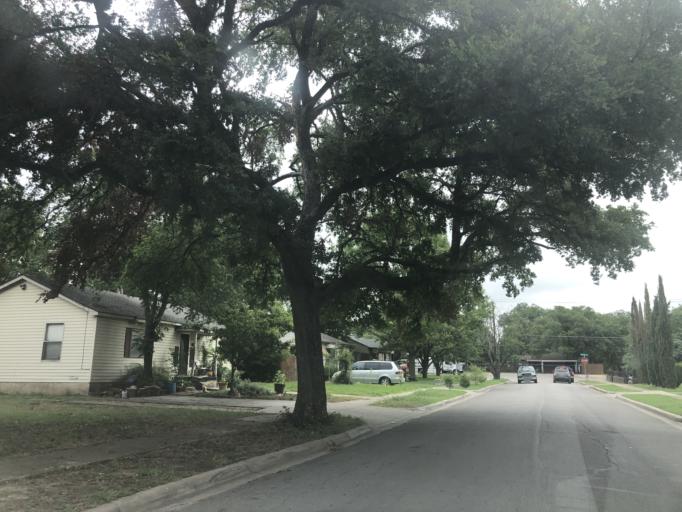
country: US
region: Texas
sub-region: Dallas County
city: University Park
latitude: 32.8713
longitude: -96.8573
